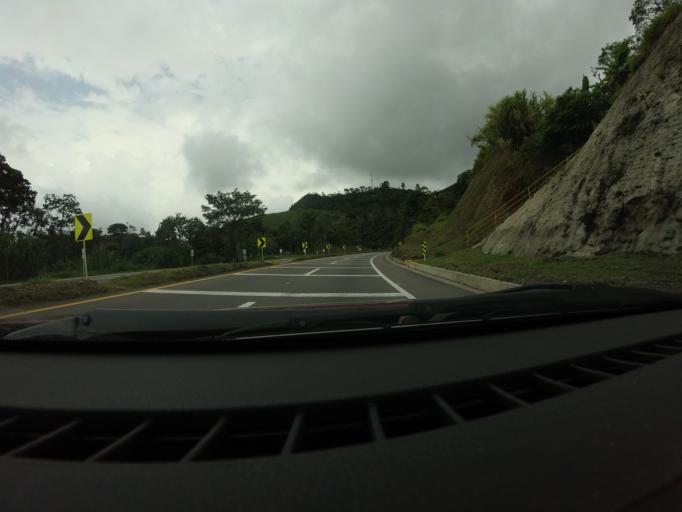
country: CO
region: Cundinamarca
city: San Francisco
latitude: 4.9656
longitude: -74.3112
